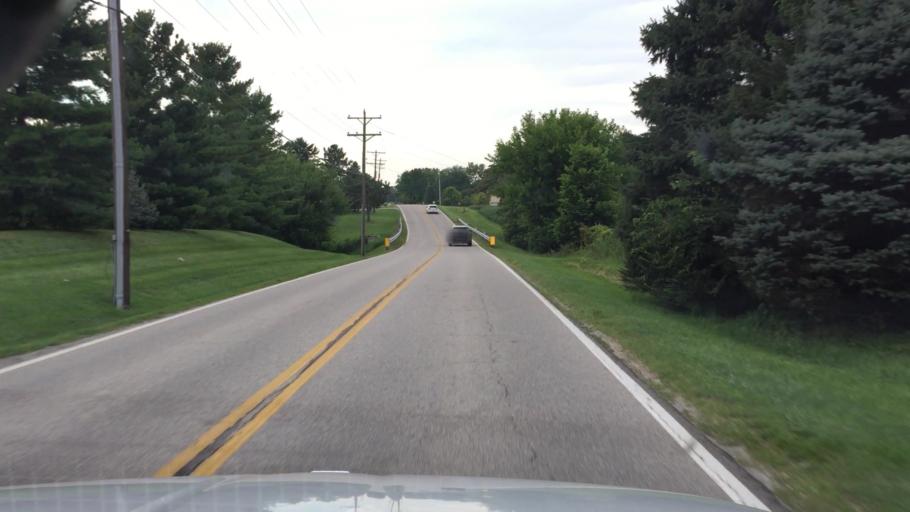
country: US
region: Ohio
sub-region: Franklin County
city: Lake Darby
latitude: 40.0275
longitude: -83.2618
